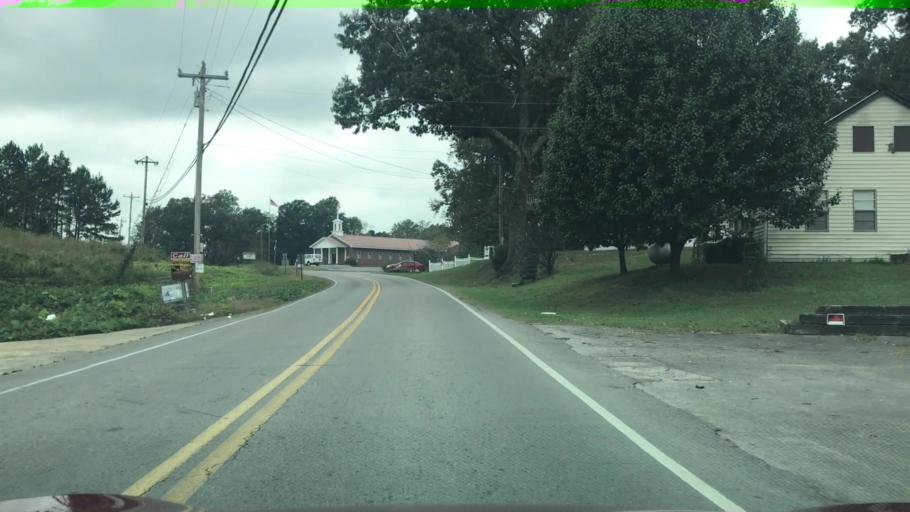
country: US
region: Alabama
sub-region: Cullman County
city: Good Hope
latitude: 34.0959
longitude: -87.0590
